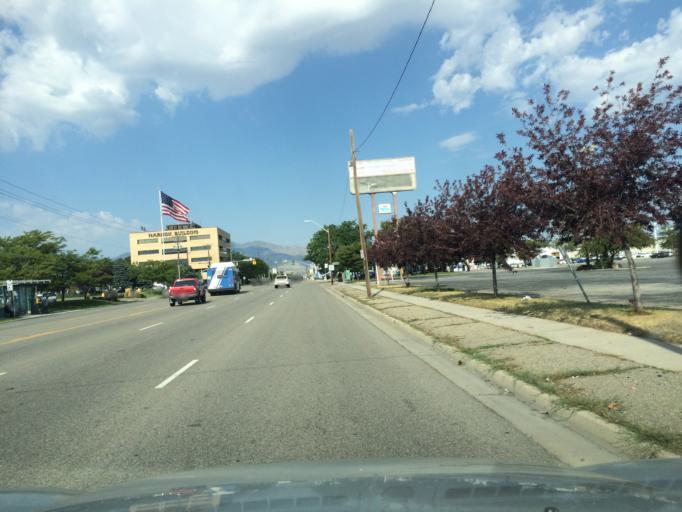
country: US
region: Utah
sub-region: Salt Lake County
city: West Valley City
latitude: 40.6968
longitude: -111.9846
